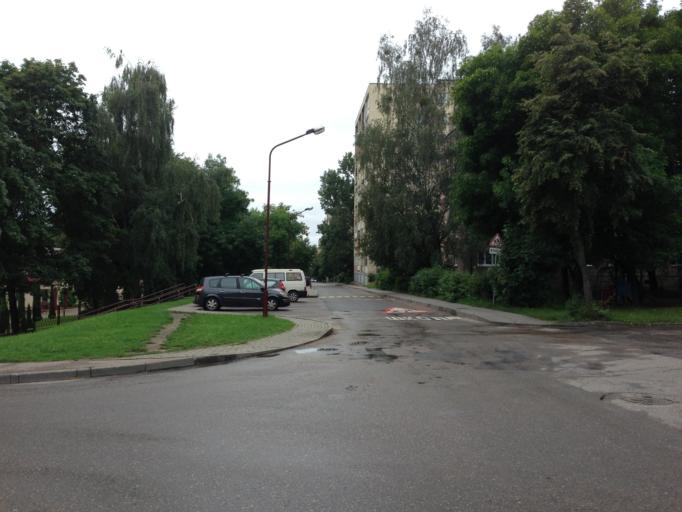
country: BY
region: Grodnenskaya
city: Hrodna
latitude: 53.6972
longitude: 23.8179
